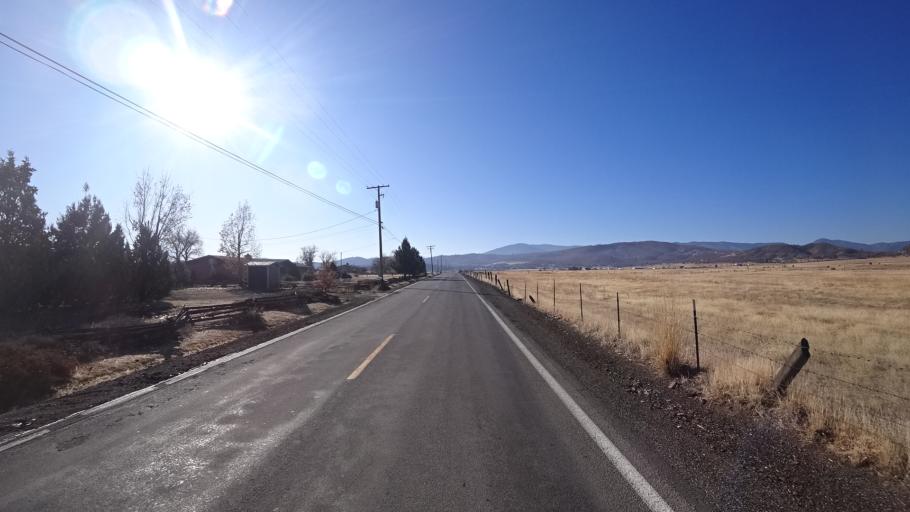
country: US
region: California
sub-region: Siskiyou County
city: Yreka
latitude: 41.7217
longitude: -122.5933
